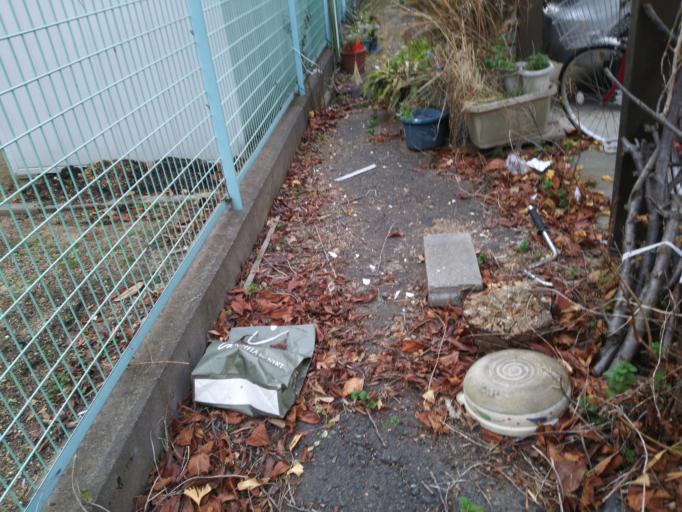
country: JP
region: Hyogo
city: Ashiya
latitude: 34.7187
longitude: 135.2591
